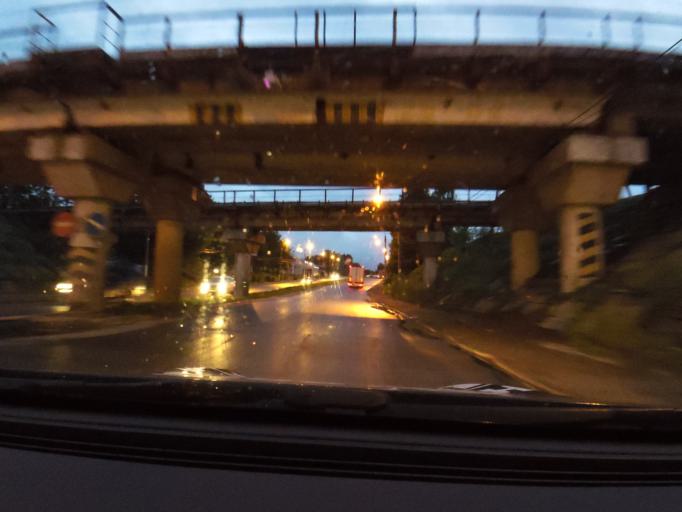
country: RU
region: Vladimir
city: Aleksandrov
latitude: 56.4042
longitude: 38.7141
